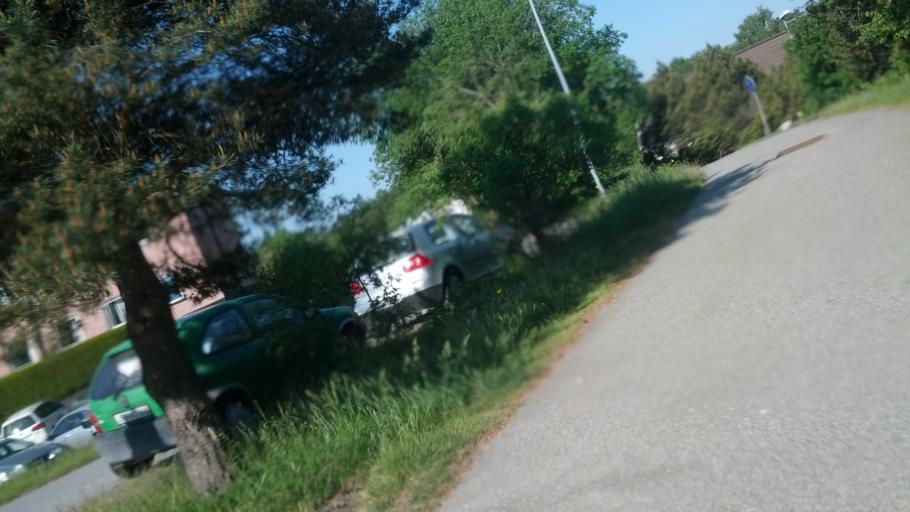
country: SE
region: Stockholm
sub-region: Taby Kommun
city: Taby
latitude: 59.4499
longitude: 18.0339
